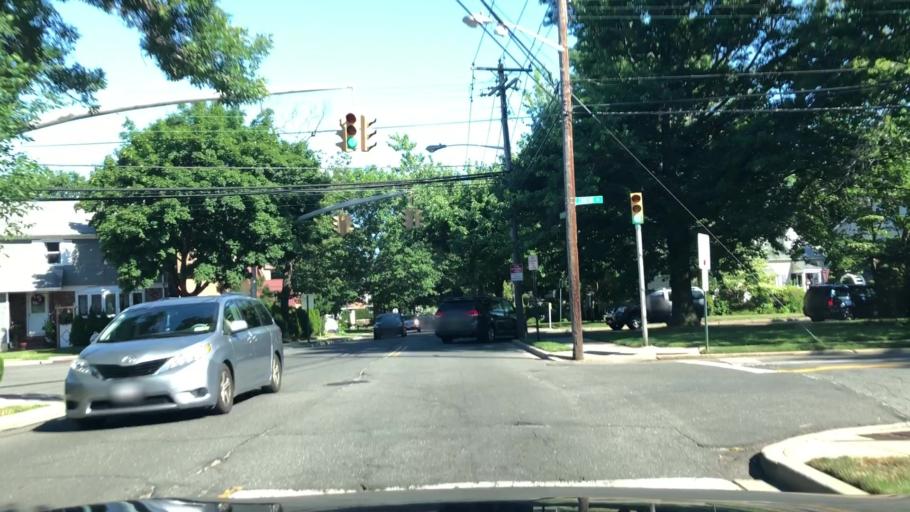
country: US
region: New York
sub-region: Nassau County
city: Floral Park
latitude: 40.7225
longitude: -73.7064
